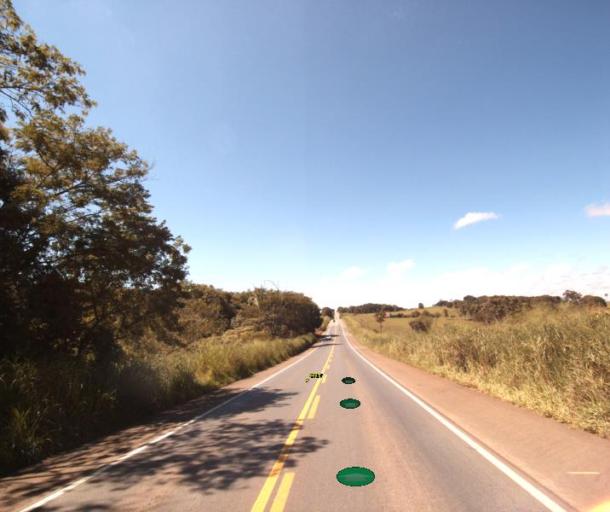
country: BR
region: Goias
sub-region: Jaragua
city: Jaragua
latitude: -15.6161
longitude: -49.3969
